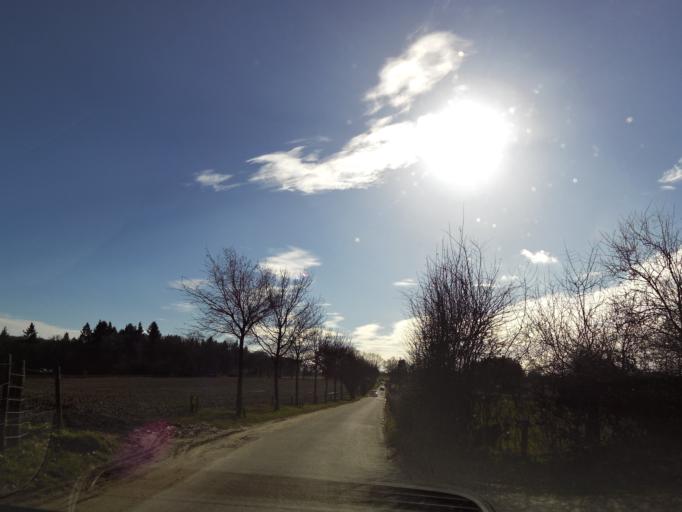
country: NL
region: Limburg
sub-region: Valkenburg aan de Geul
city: Schin op Geul
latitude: 50.7831
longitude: 5.8842
